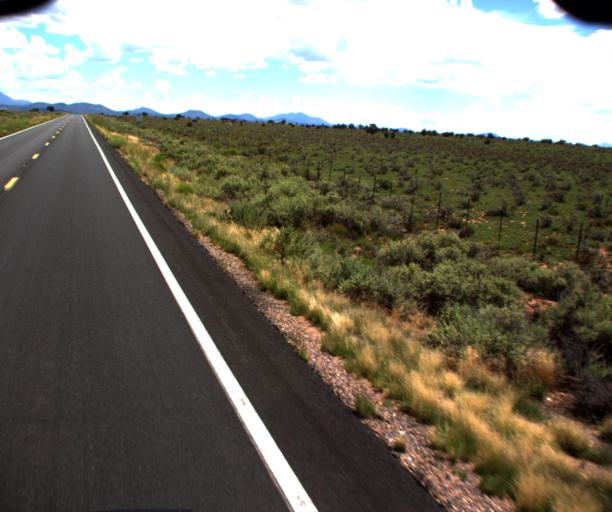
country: US
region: Arizona
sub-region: Coconino County
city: Williams
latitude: 35.6333
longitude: -112.1201
